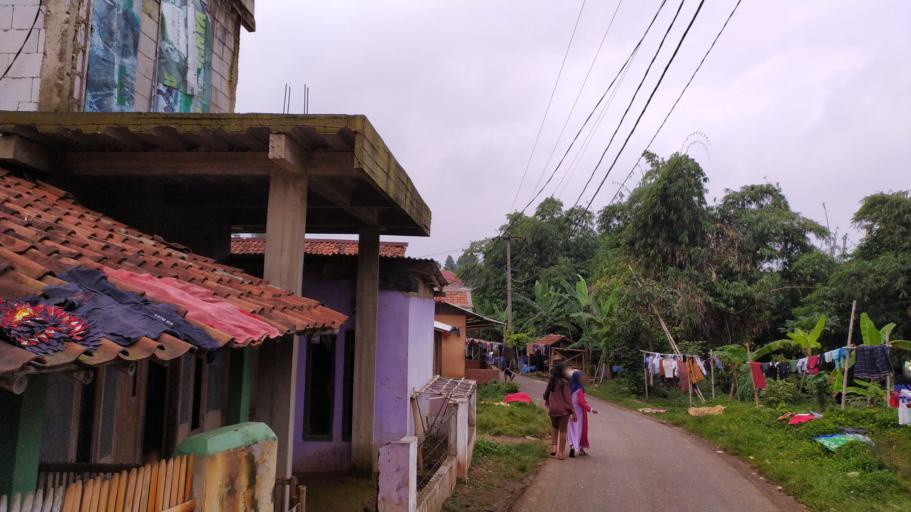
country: ID
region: West Java
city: Ciampea
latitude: -6.6296
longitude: 106.7063
